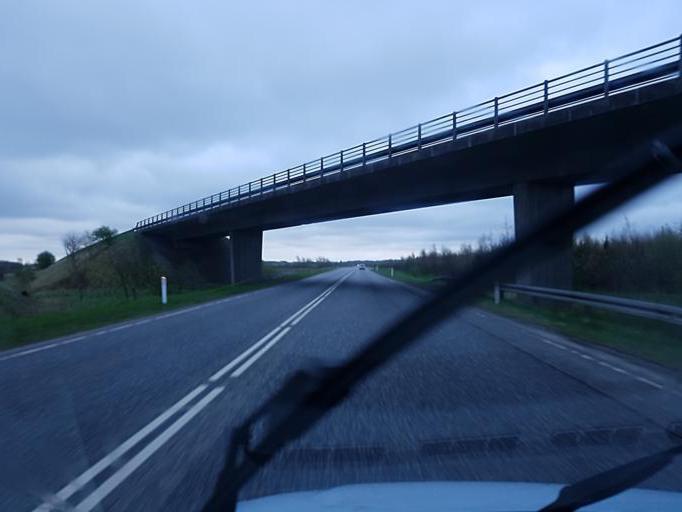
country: DK
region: South Denmark
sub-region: Esbjerg Kommune
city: Bramming
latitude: 55.4050
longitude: 8.7244
